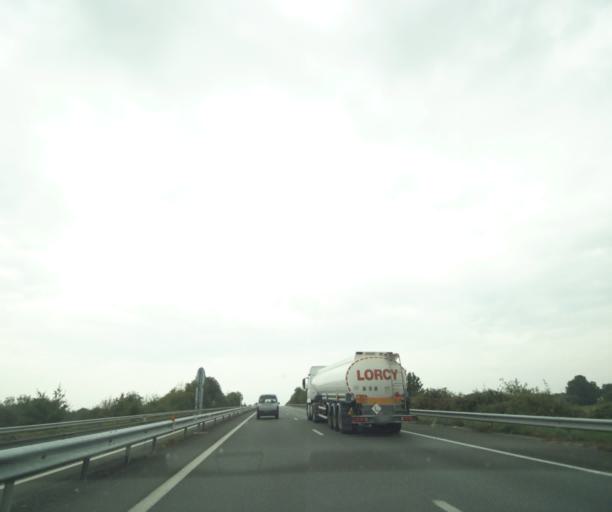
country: FR
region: Pays de la Loire
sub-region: Departement de la Vendee
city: Bournezeau
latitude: 46.6481
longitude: -1.1514
